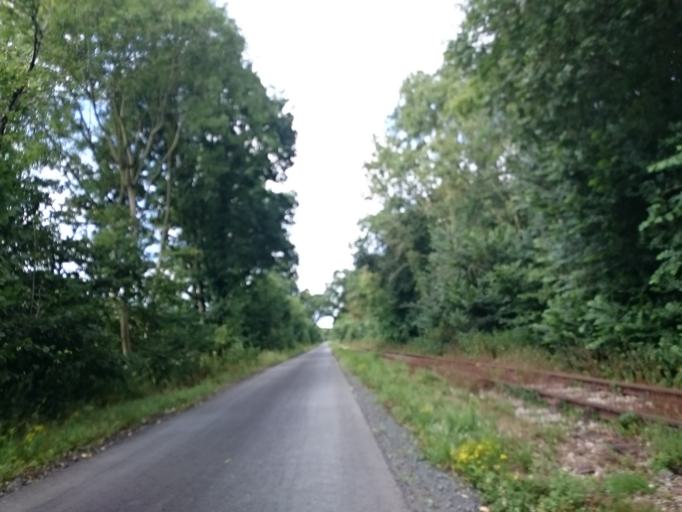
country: FR
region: Lower Normandy
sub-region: Departement du Calvados
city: Sainte-Honorine-du-Fay
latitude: 49.0385
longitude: -0.4645
